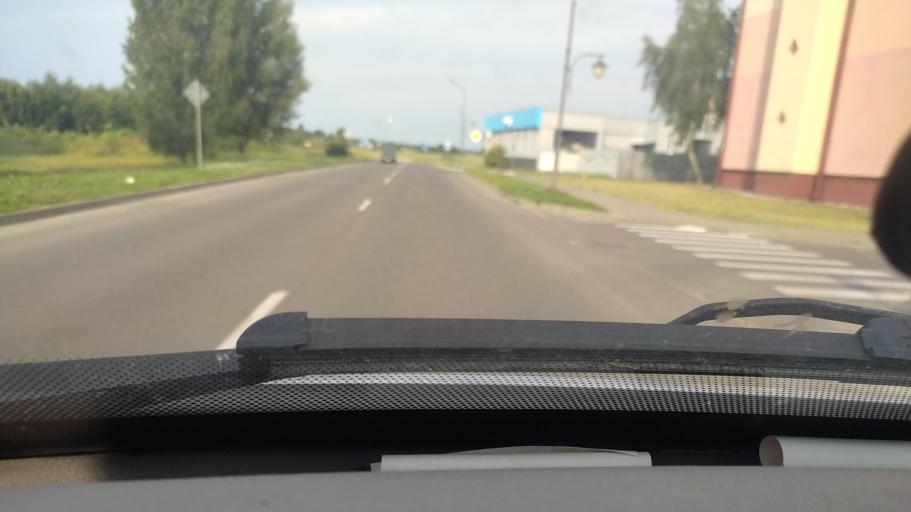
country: BY
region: Brest
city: Byaroza
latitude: 52.5378
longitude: 24.9734
